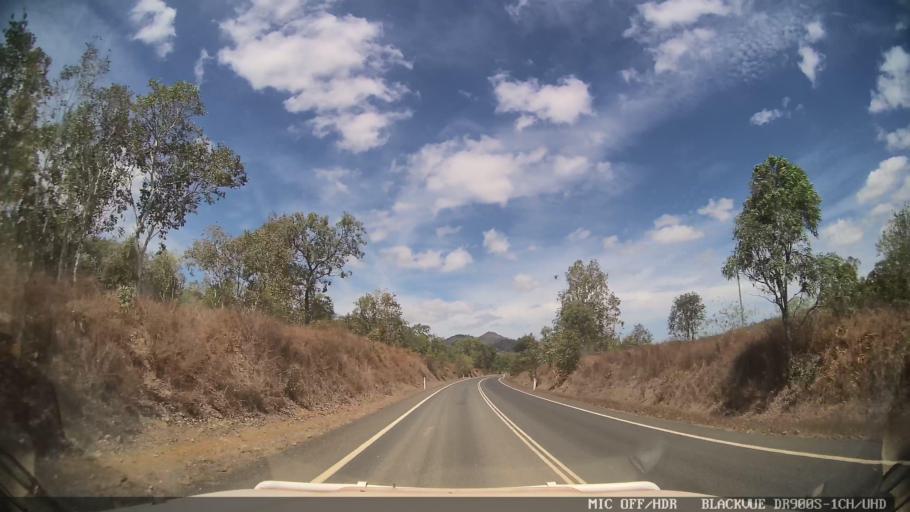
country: AU
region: Queensland
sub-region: Cook
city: Cooktown
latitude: -15.6153
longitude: 145.2209
